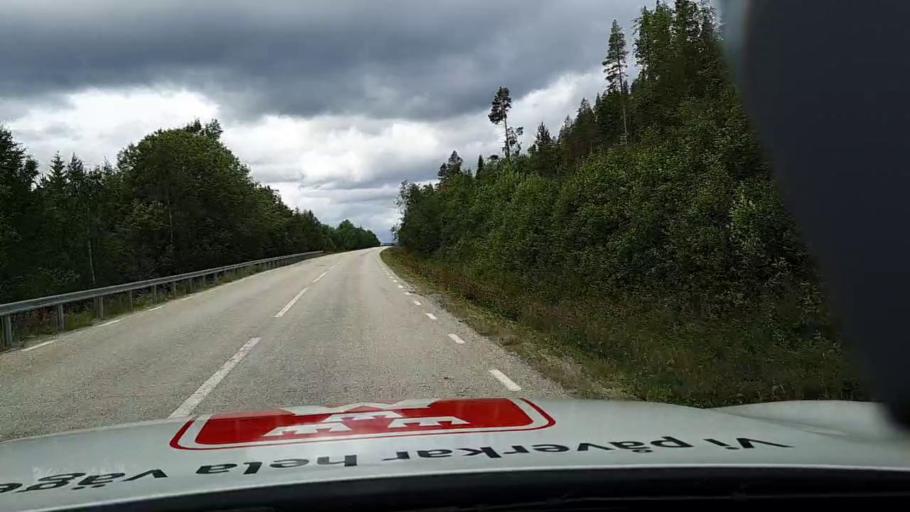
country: SE
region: Jaemtland
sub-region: Are Kommun
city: Jarpen
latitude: 62.8011
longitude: 13.5596
